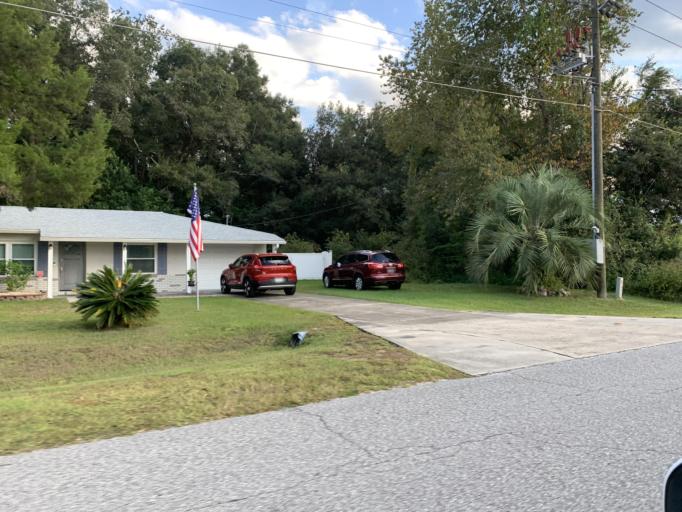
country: US
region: Florida
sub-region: Marion County
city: Silver Springs Shores
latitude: 29.1590
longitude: -82.0454
